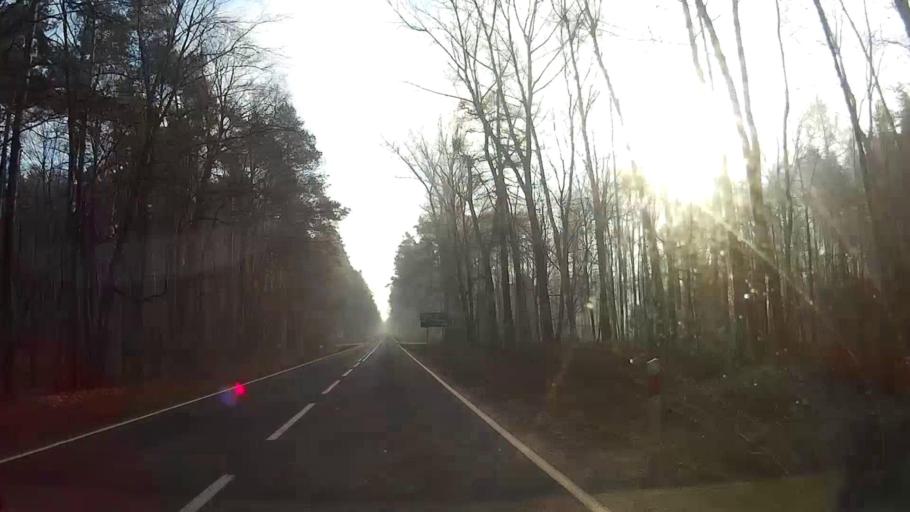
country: PL
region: Lesser Poland Voivodeship
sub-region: Powiat chrzanowski
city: Metkow
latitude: 50.0756
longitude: 19.3863
